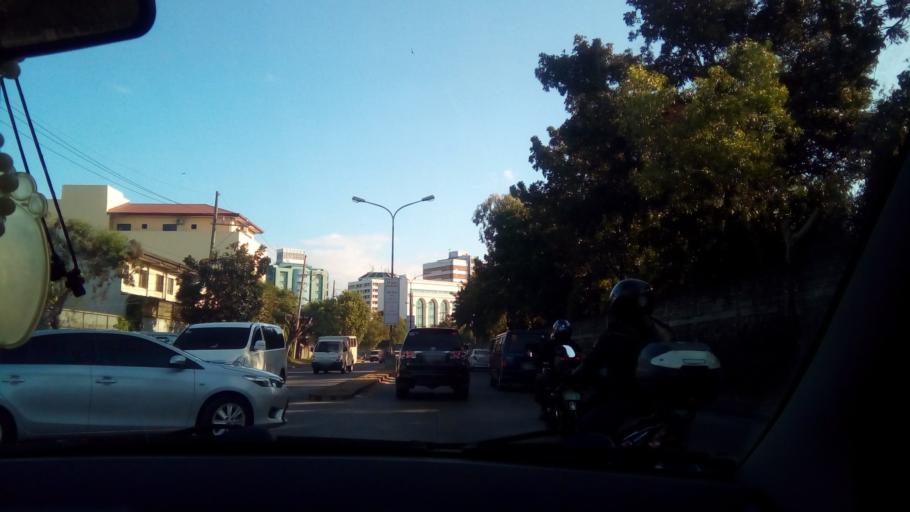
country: PH
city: Sambayanihan People's Village
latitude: 14.4236
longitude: 121.0226
